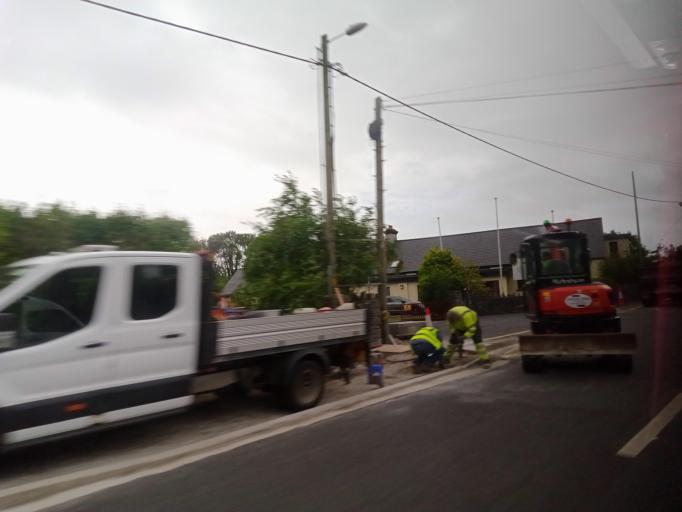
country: IE
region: Munster
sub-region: Waterford
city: Dungarvan
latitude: 52.0475
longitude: -7.5760
